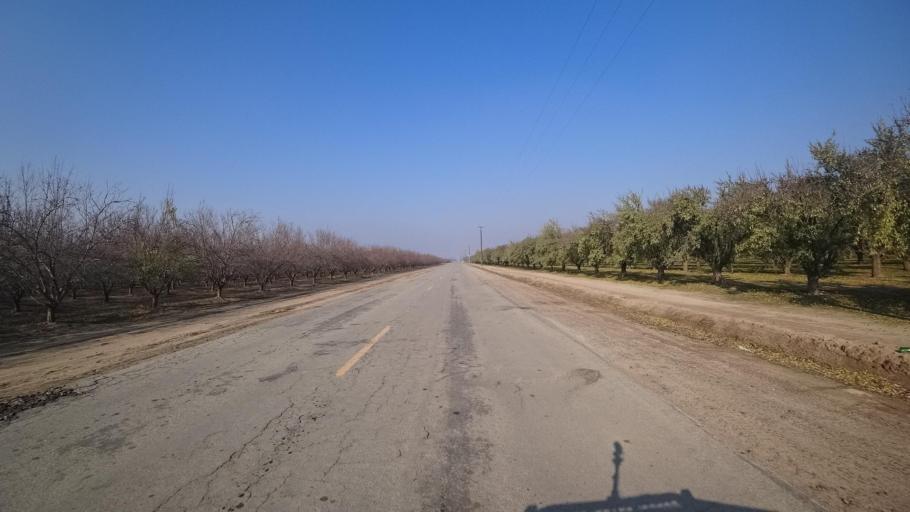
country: US
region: California
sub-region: Kern County
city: Greenfield
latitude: 35.2023
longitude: -119.0392
